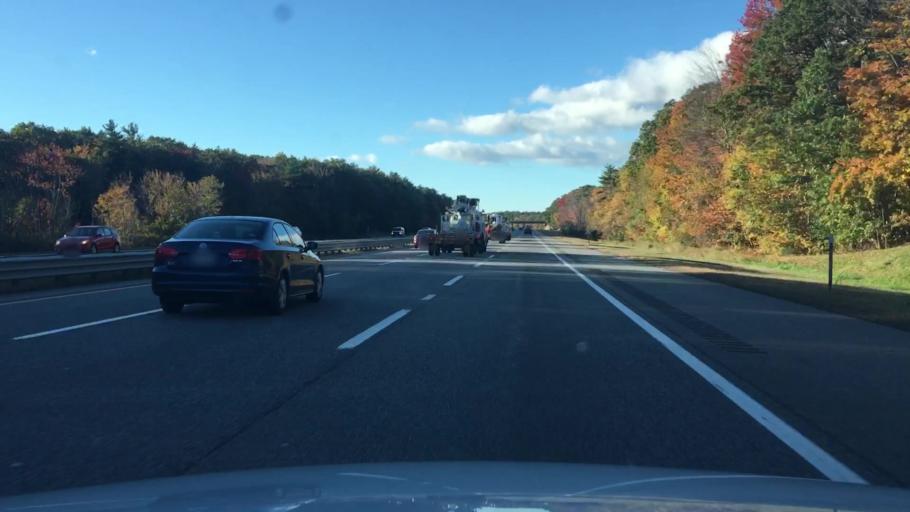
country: US
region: Maine
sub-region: York County
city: Cape Neddick
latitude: 43.2117
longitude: -70.6412
